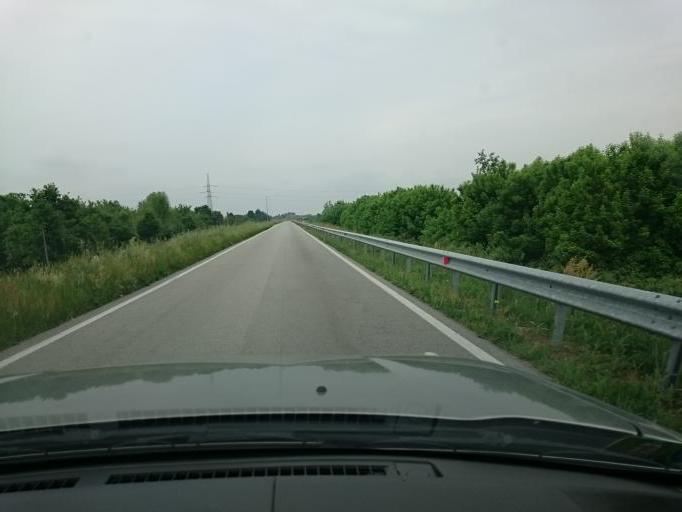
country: IT
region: Veneto
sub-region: Provincia di Padova
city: Bovolenta
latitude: 45.2707
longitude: 11.9421
